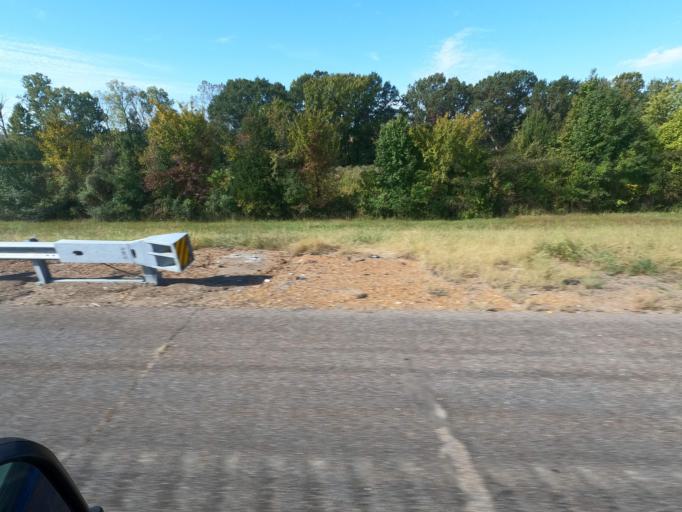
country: US
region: Tennessee
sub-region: Shelby County
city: Arlington
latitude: 35.2807
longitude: -89.6807
